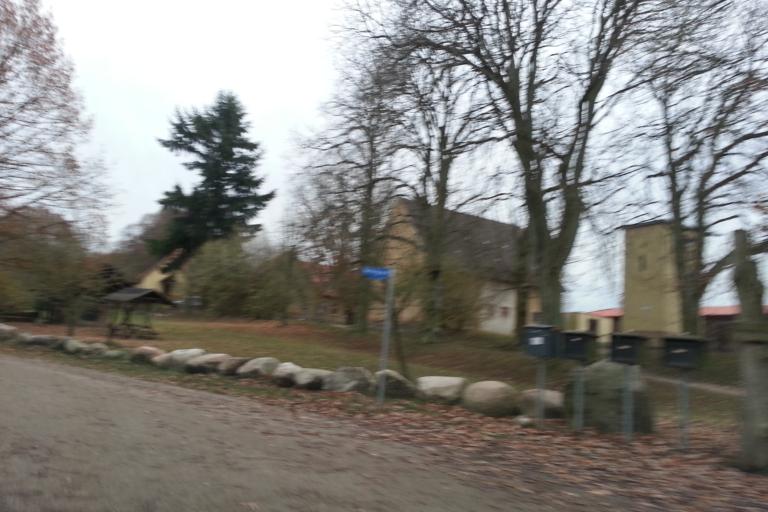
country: DE
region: Mecklenburg-Vorpommern
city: Ferdinandshof
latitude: 53.5873
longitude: 13.8369
